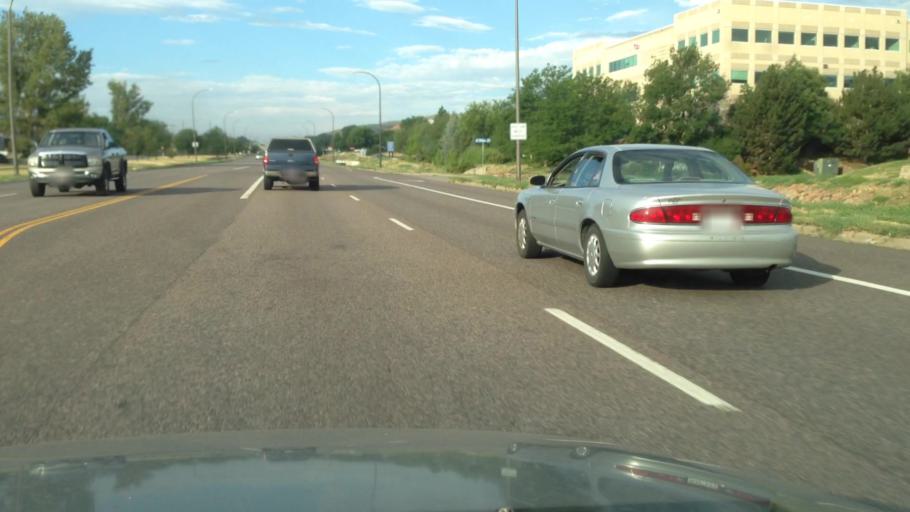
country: US
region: Colorado
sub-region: Jefferson County
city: West Pleasant View
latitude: 39.7074
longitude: -105.1356
